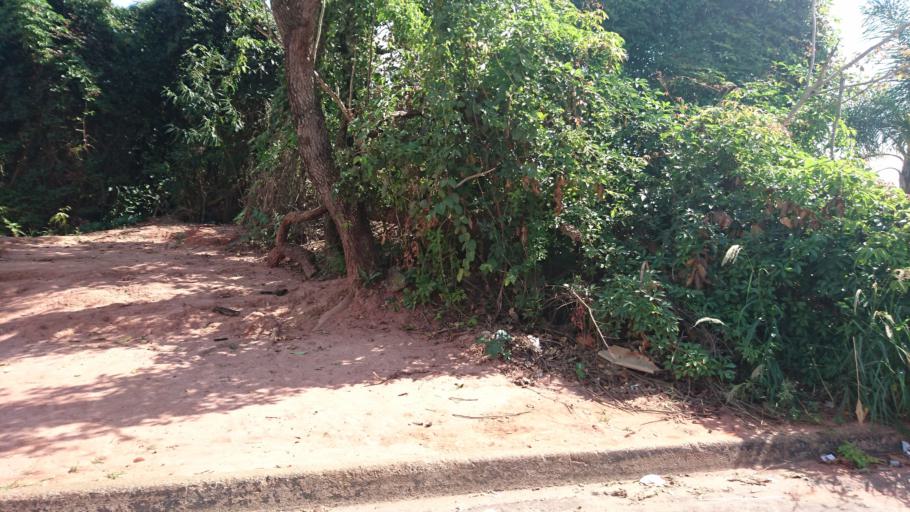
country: BR
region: Sao Paulo
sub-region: Casa Branca
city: Casa Branca
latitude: -21.7883
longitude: -47.0916
